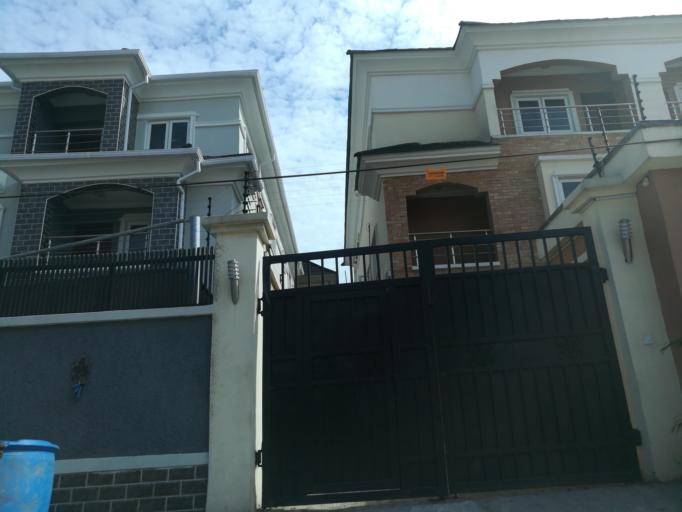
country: NG
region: Lagos
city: Ojota
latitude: 6.5775
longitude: 3.3667
